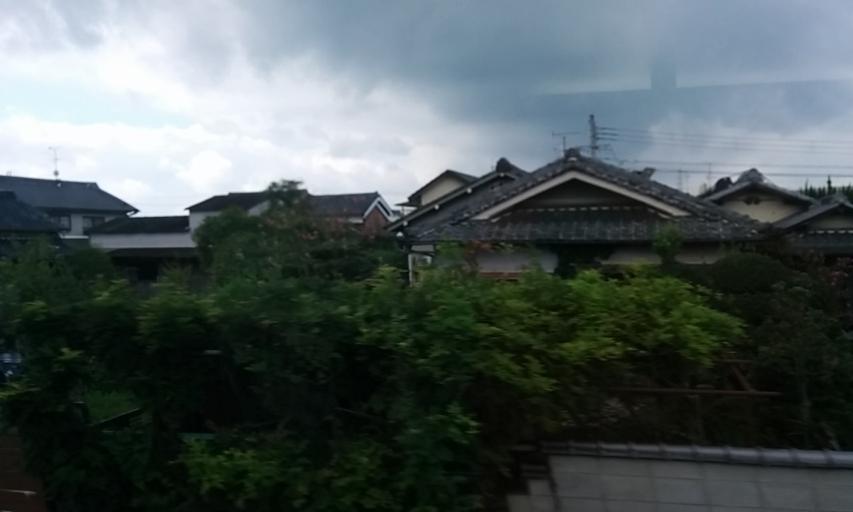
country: JP
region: Nara
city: Tawaramoto
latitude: 34.5755
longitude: 135.7855
